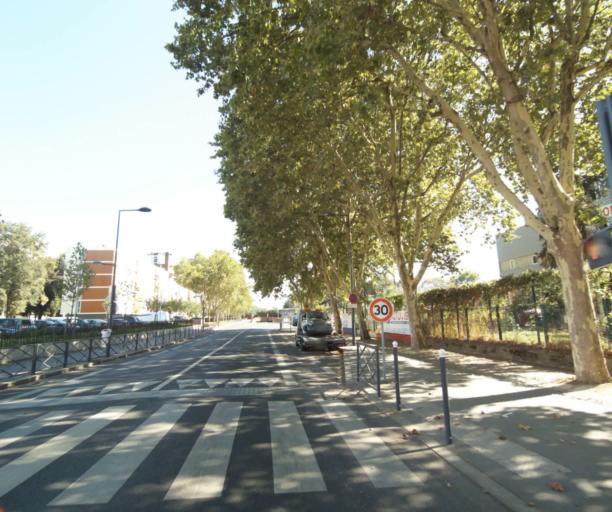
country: FR
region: Ile-de-France
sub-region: Departement des Hauts-de-Seine
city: Villeneuve-la-Garenne
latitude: 48.9326
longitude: 2.3253
